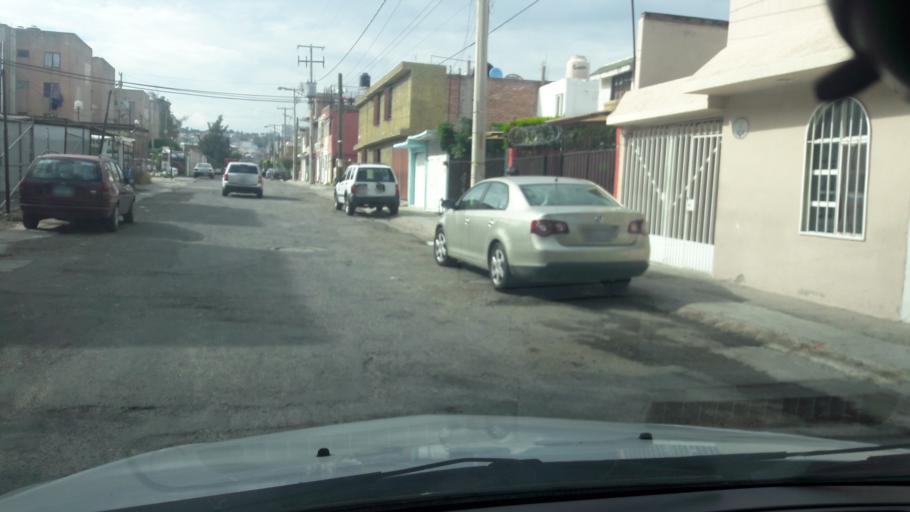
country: MX
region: Guanajuato
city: Leon
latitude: 21.1432
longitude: -101.6975
